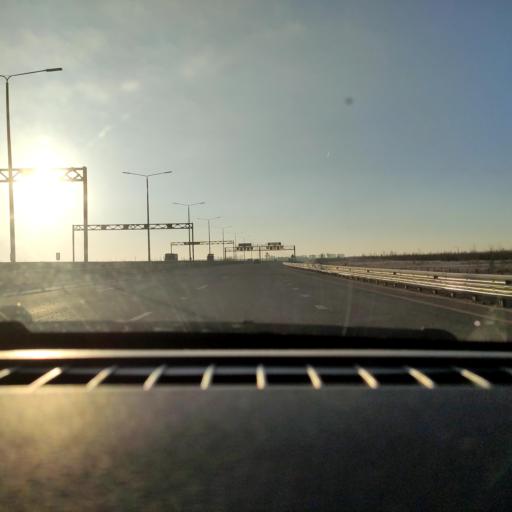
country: RU
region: Voronezj
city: Somovo
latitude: 51.7761
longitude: 39.2993
